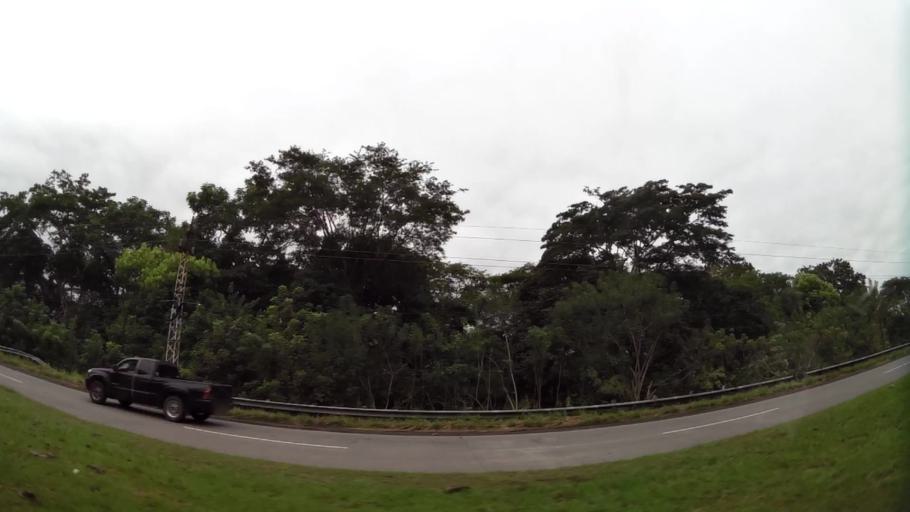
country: PA
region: Chiriqui
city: Tijera
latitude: 8.4782
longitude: -82.5522
